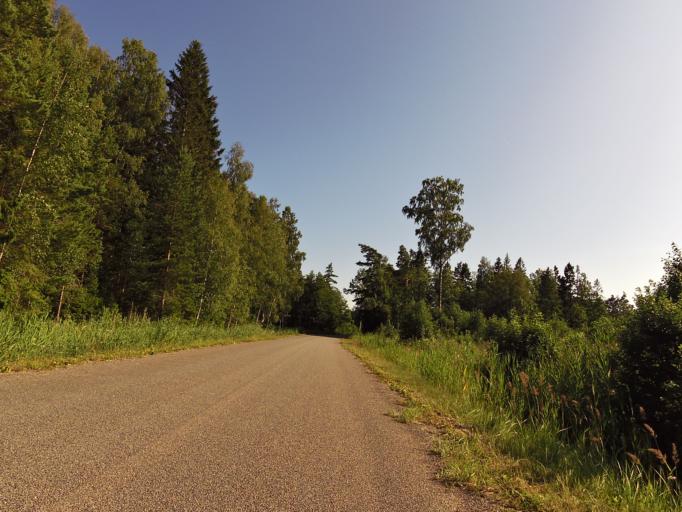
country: EE
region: Hiiumaa
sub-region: Kaerdla linn
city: Kardla
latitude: 58.8995
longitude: 22.2794
